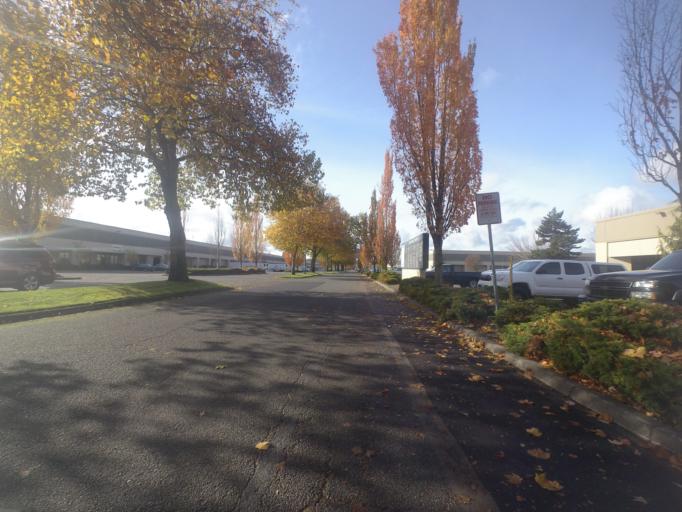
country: US
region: Washington
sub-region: Pierce County
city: Lakewood
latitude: 47.1711
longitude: -122.4936
